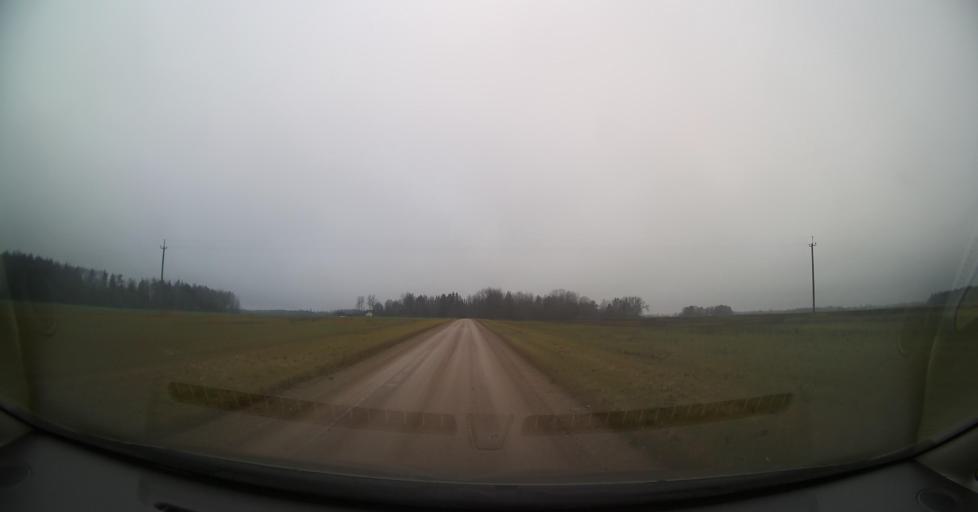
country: EE
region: Tartu
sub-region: Tartu linn
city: Tartu
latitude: 58.3754
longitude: 26.9306
